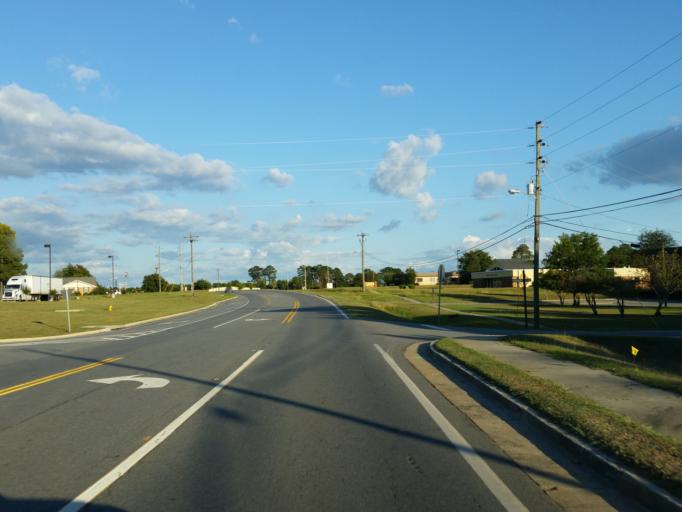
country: US
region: Georgia
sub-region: Dooly County
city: Vienna
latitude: 32.0875
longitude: -83.7745
